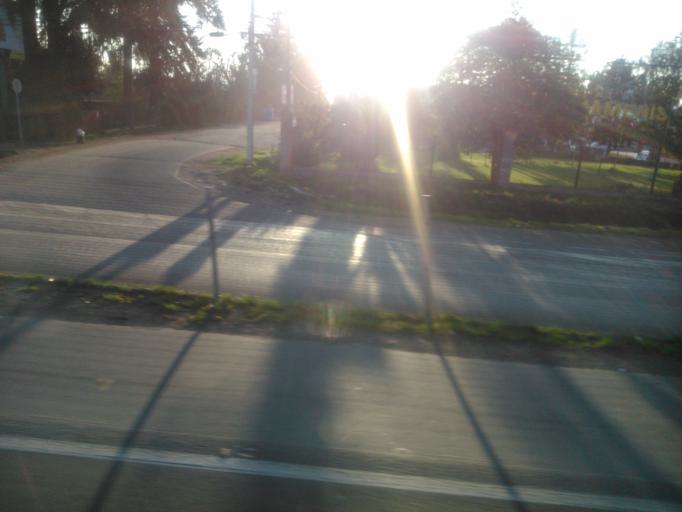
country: CL
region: Santiago Metropolitan
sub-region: Provincia de Maipo
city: Buin
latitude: -33.7678
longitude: -70.7428
